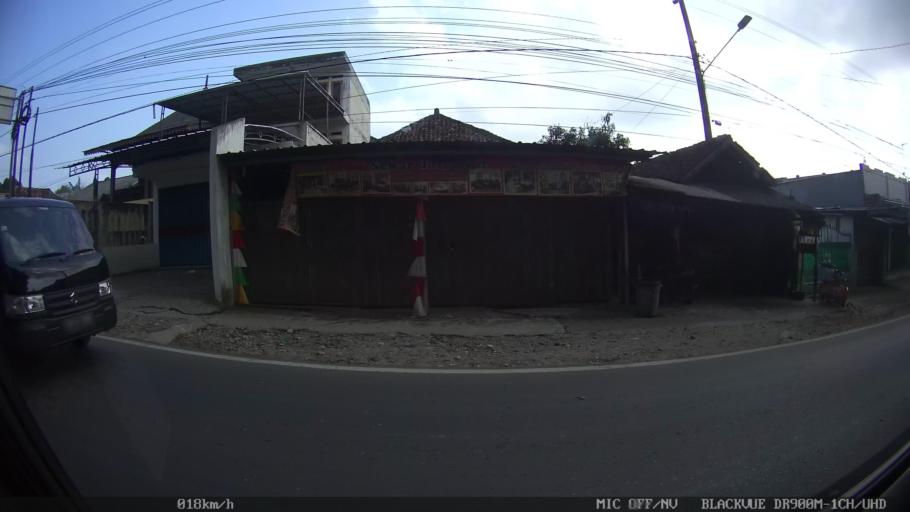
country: ID
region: Lampung
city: Kedaton
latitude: -5.3926
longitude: 105.2291
